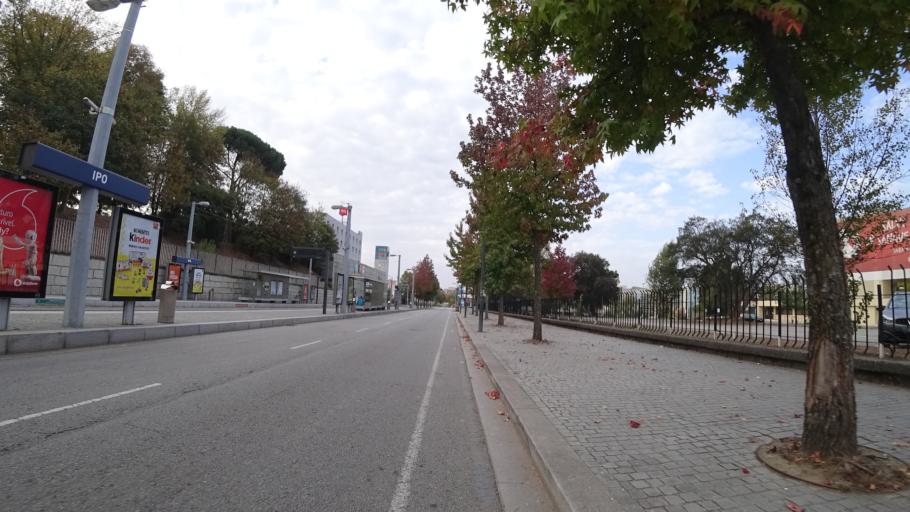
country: PT
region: Porto
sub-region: Matosinhos
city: Sao Mamede de Infesta
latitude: 41.1816
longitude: -8.6045
